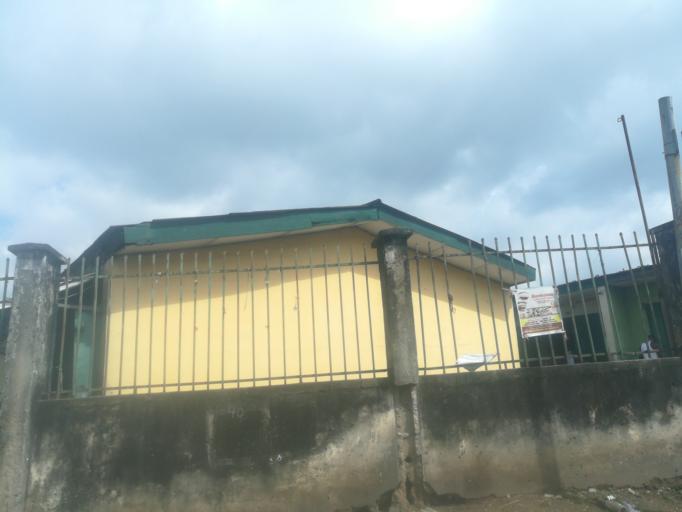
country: NG
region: Lagos
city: Somolu
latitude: 6.5471
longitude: 3.3736
